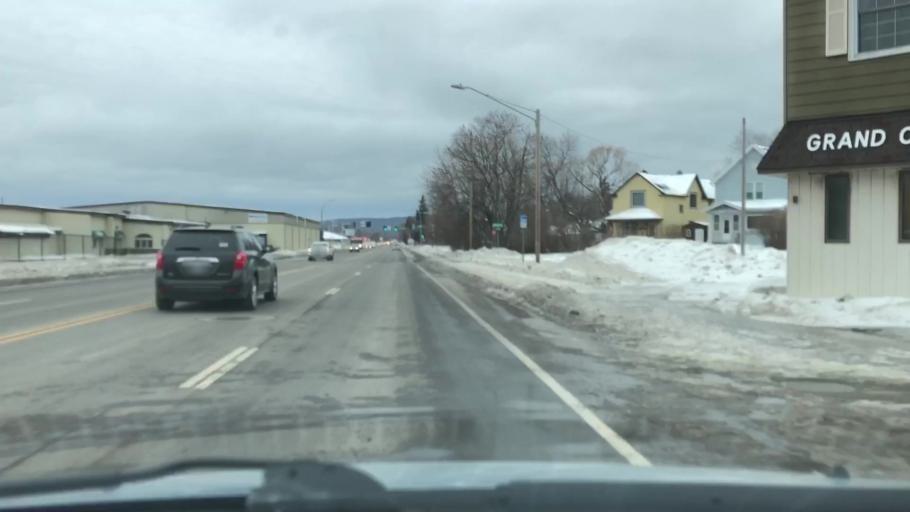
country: US
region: Minnesota
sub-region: Saint Louis County
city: Proctor
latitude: 46.7328
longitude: -92.1779
